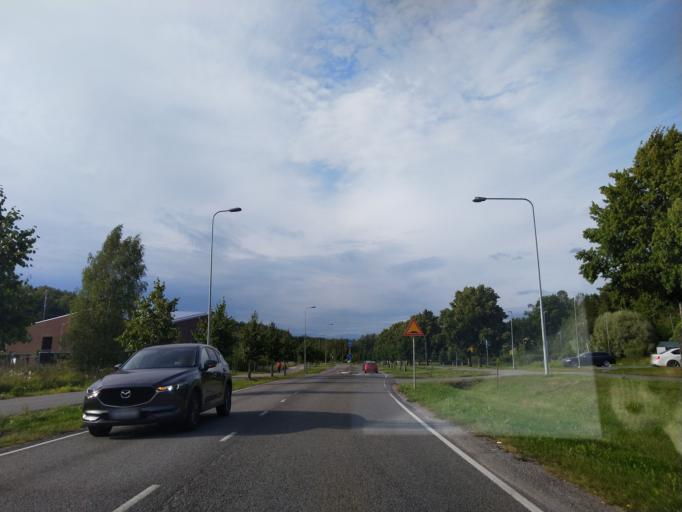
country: FI
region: Varsinais-Suomi
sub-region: Turku
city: Turku
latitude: 60.4185
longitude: 22.2286
